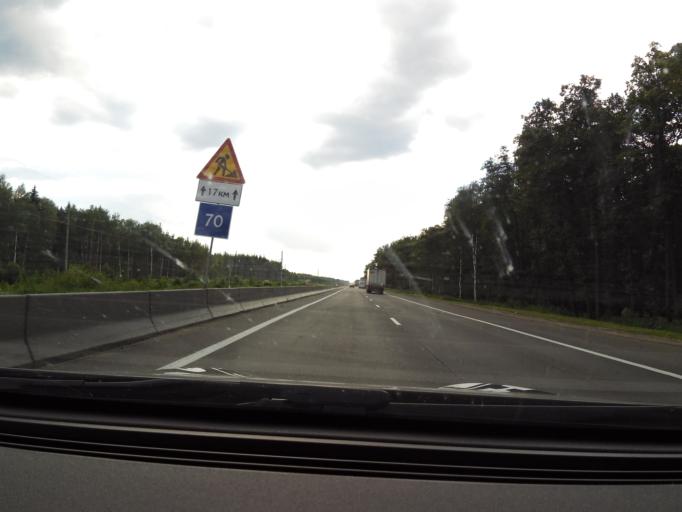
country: RU
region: Nizjnij Novgorod
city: Smolino
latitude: 56.2842
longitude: 43.1467
